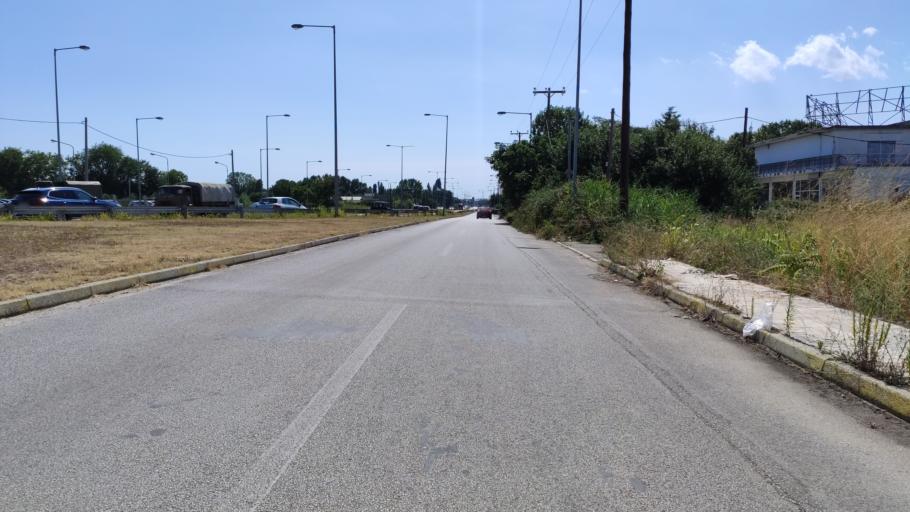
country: GR
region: East Macedonia and Thrace
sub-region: Nomos Rodopis
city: Komotini
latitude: 41.1146
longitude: 25.3801
